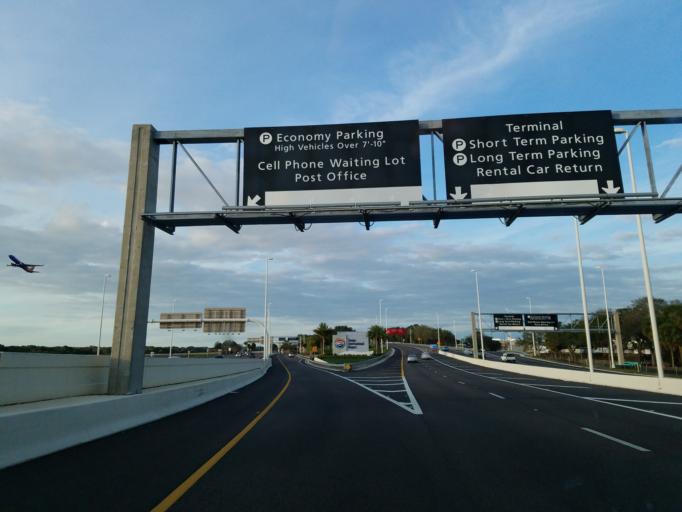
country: US
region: Florida
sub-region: Hillsborough County
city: Town 'n' Country
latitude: 27.9633
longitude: -82.5391
